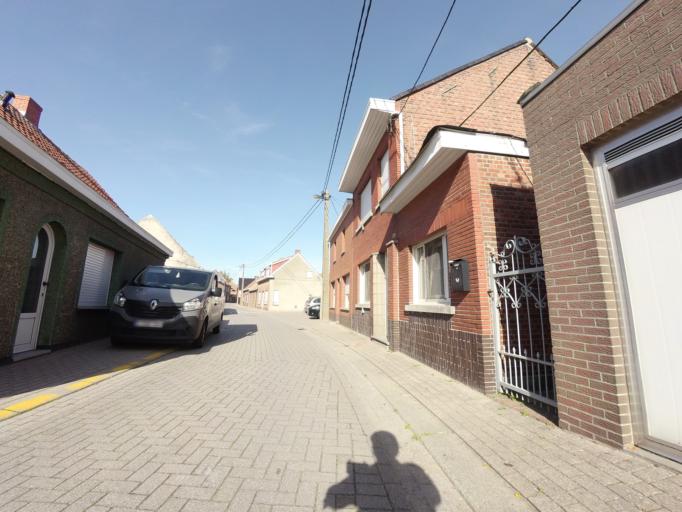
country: BE
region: Flanders
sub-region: Provincie Antwerpen
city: Stabroek
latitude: 51.3583
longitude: 4.3097
